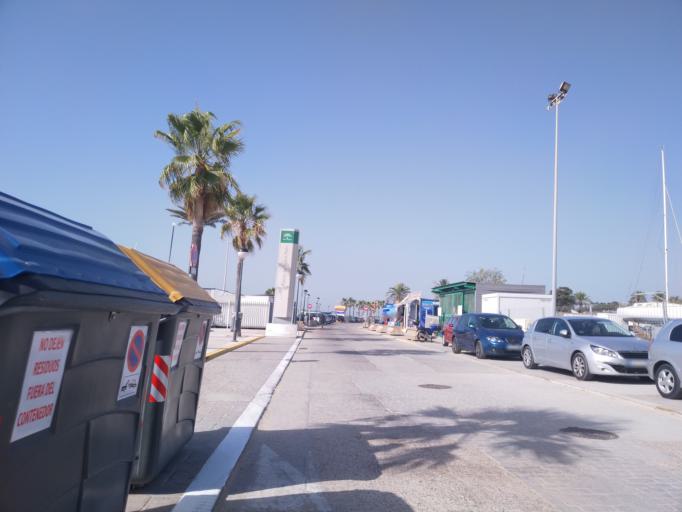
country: ES
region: Andalusia
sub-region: Provincia de Cadiz
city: Chiclana de la Frontera
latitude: 36.3940
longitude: -6.2090
